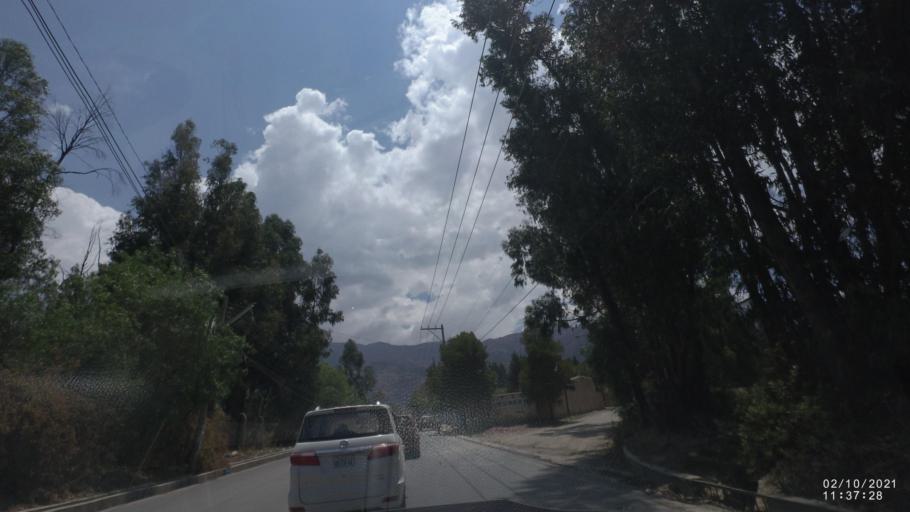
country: BO
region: Cochabamba
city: Cochabamba
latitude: -17.3436
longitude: -66.2228
